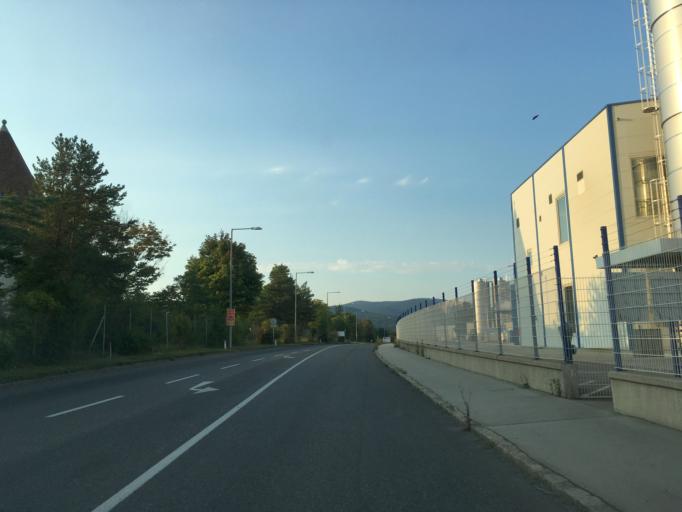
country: AT
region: Lower Austria
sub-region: Politischer Bezirk Baden
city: Baden
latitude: 47.9916
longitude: 16.2253
